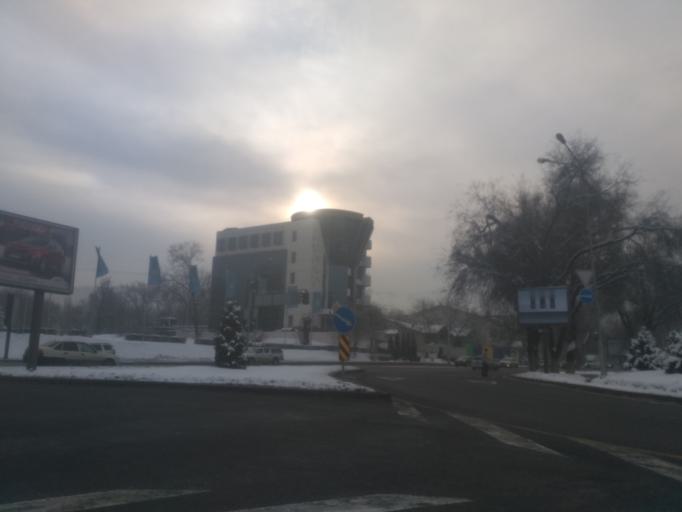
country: KZ
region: Almaty Qalasy
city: Almaty
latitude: 43.2287
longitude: 76.9603
